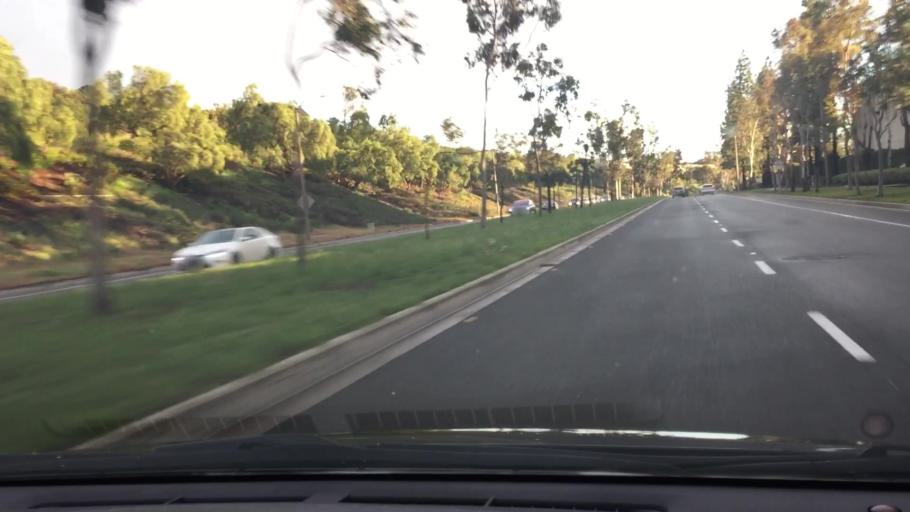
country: US
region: California
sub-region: Orange County
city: North Tustin
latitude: 33.7671
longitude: -117.7604
